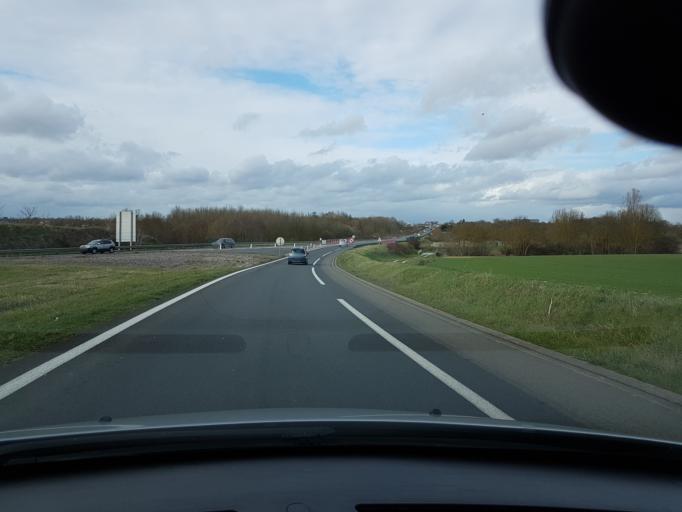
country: FR
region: Centre
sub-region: Departement du Cher
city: Saint-Germain-du-Puy
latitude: 47.0856
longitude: 2.4432
